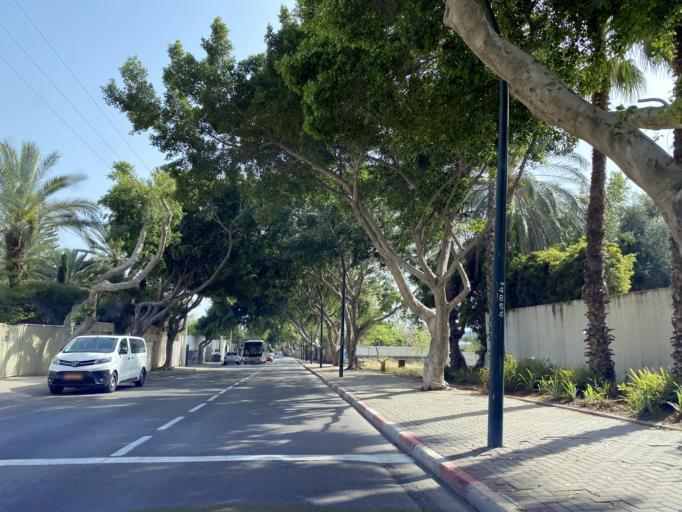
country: IL
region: Tel Aviv
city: Herzliya Pituah
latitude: 32.1711
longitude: 34.8070
